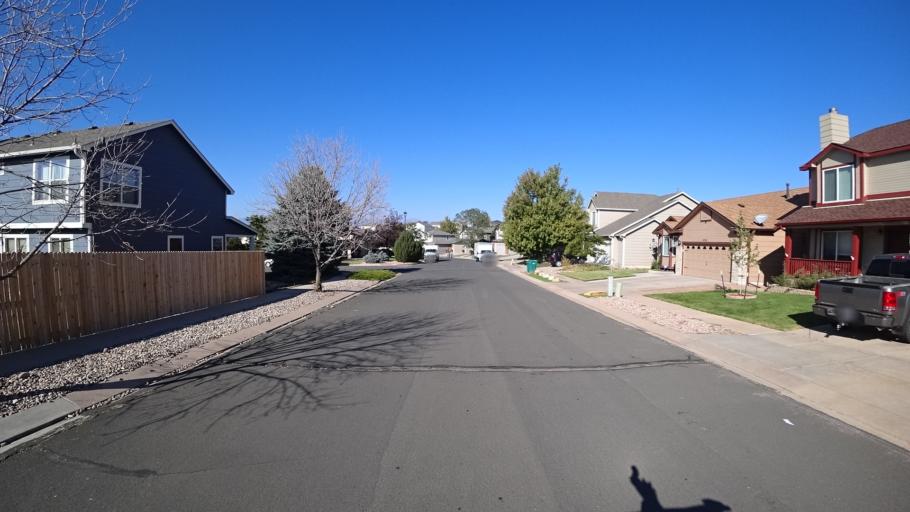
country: US
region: Colorado
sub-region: El Paso County
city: Cimarron Hills
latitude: 38.8910
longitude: -104.6962
